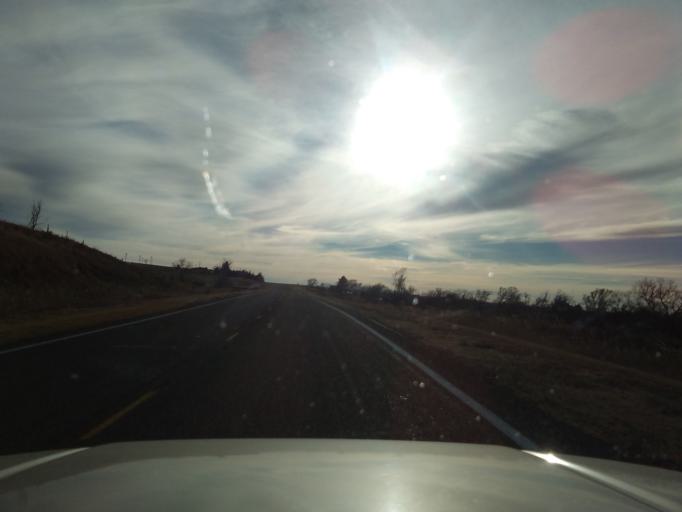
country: US
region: Kansas
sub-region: Norton County
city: Norton
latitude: 39.7388
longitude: -100.1727
